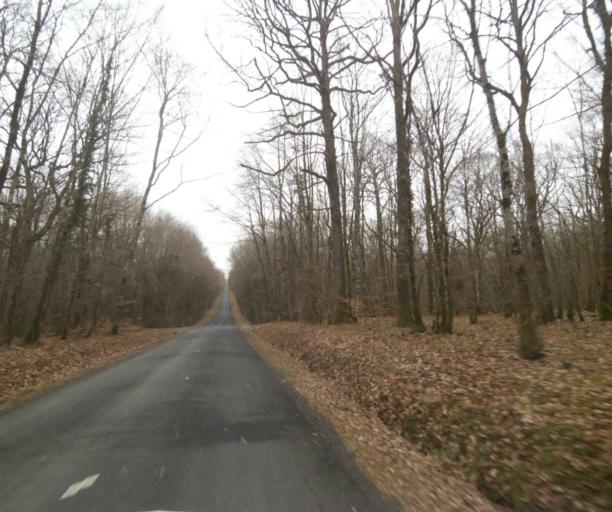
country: FR
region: Champagne-Ardenne
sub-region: Departement de la Haute-Marne
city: Bienville
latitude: 48.5569
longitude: 5.0028
